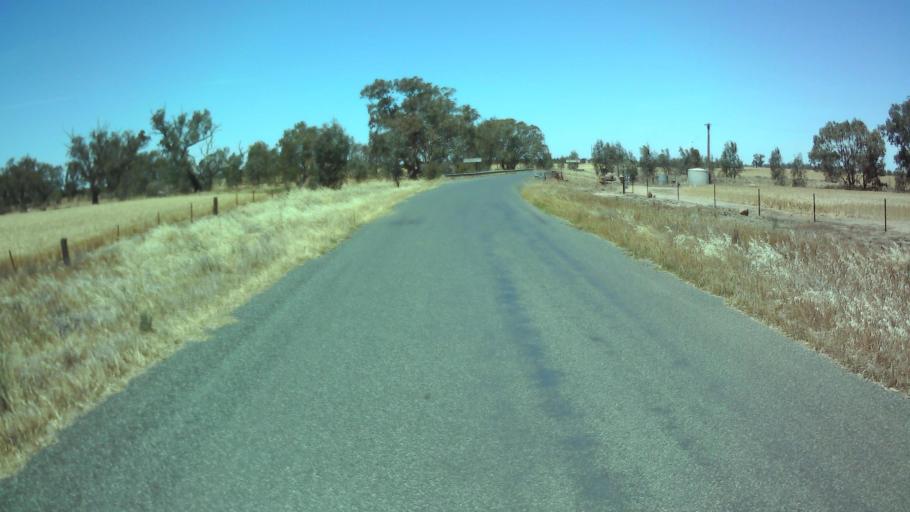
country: AU
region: New South Wales
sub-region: Weddin
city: Grenfell
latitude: -34.0380
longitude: 147.7898
